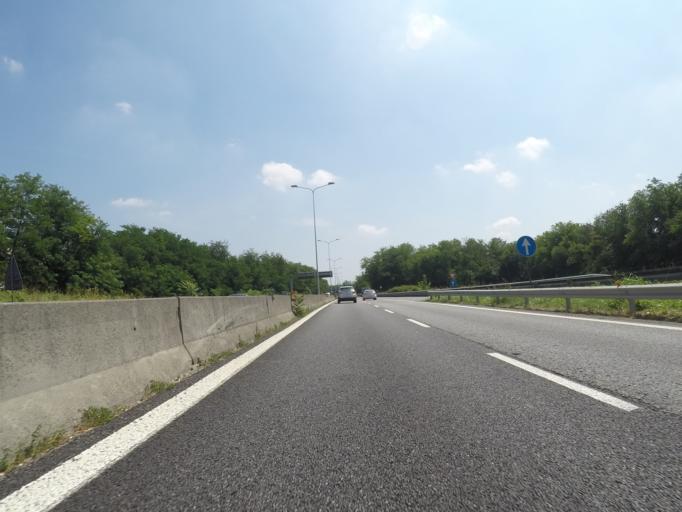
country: IT
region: Lombardy
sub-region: Provincia di Varese
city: Gallarate
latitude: 45.6422
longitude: 8.7972
